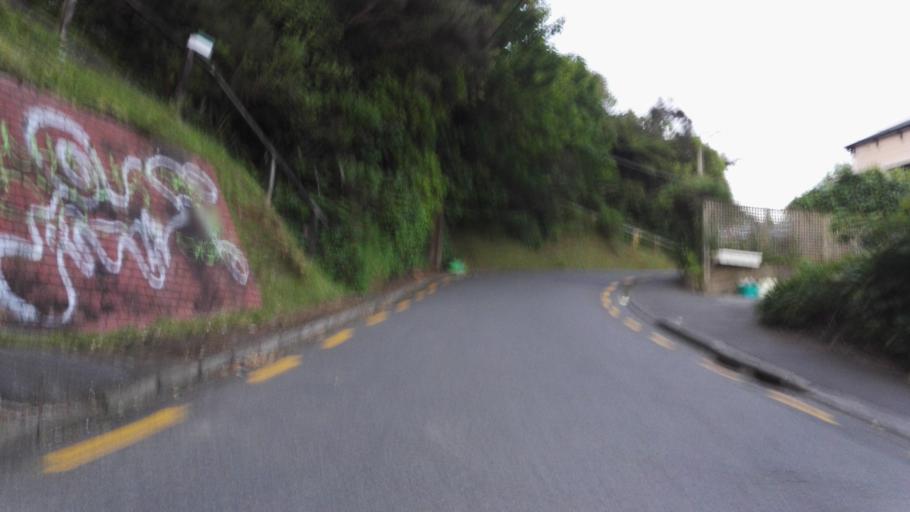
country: NZ
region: Wellington
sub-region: Wellington City
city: Kelburn
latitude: -41.2936
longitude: 174.7658
